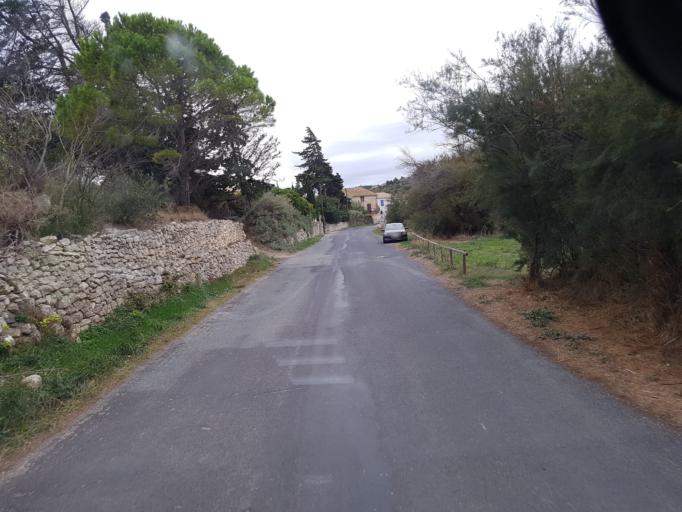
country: FR
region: Languedoc-Roussillon
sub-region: Departement de l'Aude
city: Peyriac-de-Mer
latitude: 43.1242
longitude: 2.9907
